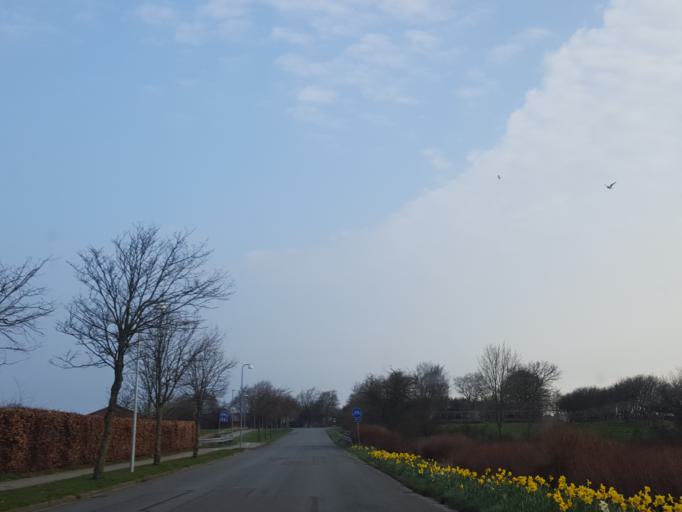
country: DK
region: South Denmark
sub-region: Esbjerg Kommune
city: Bramming
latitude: 55.4826
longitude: 8.7029
